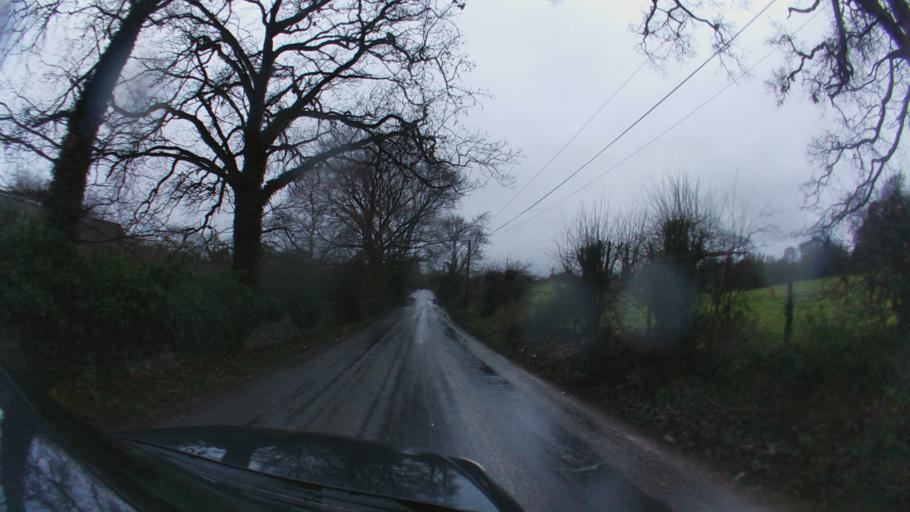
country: IE
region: Leinster
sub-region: County Carlow
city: Bagenalstown
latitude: 52.6567
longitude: -6.9904
